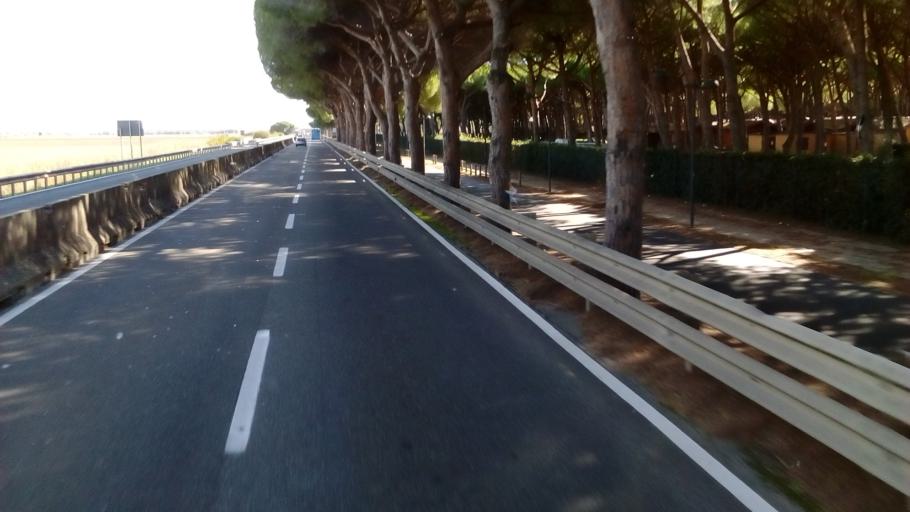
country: IT
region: Tuscany
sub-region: Provincia di Grosseto
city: Fonteblanda
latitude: 42.5324
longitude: 11.1862
